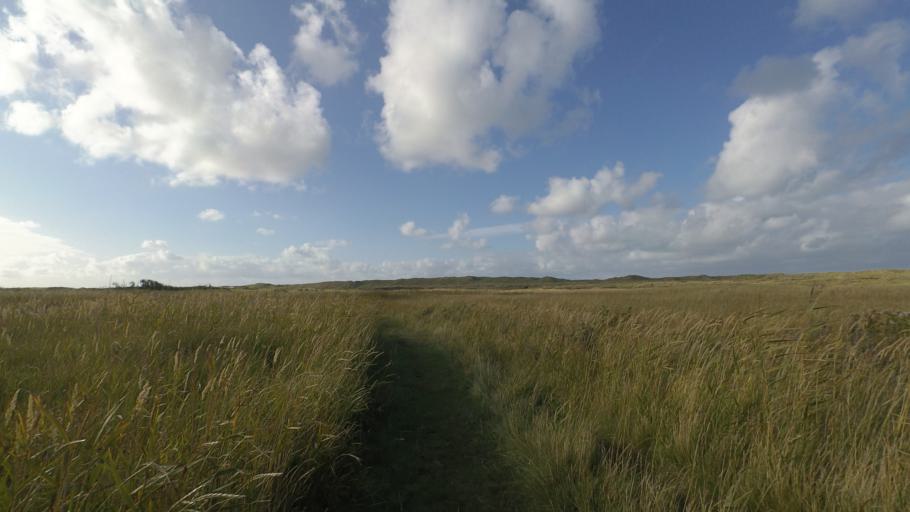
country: NL
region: Friesland
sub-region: Gemeente Dongeradeel
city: Ternaard
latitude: 53.4627
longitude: 5.9170
